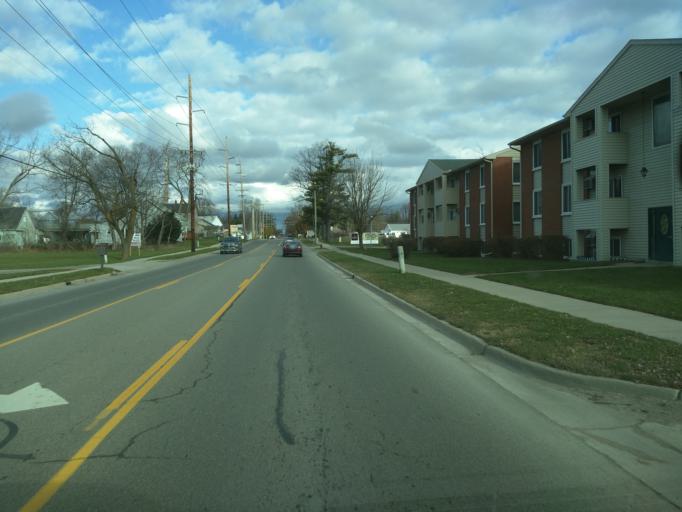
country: US
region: Michigan
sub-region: Livingston County
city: Fowlerville
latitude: 42.6540
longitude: -84.0728
